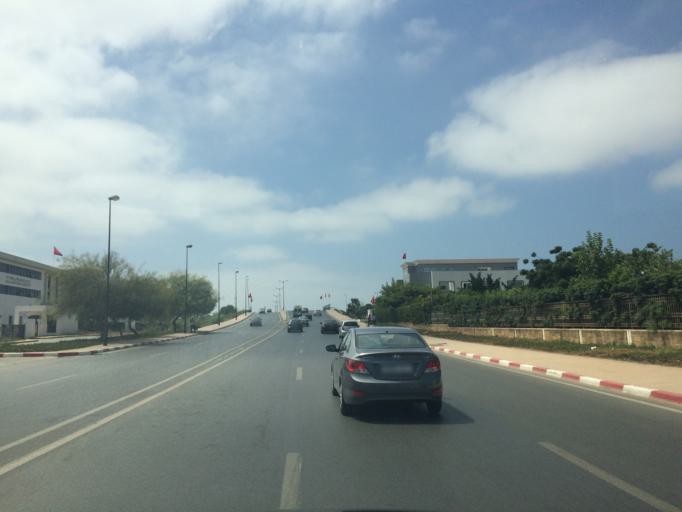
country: MA
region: Rabat-Sale-Zemmour-Zaer
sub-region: Skhirate-Temara
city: Temara
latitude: 33.9706
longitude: -6.8768
